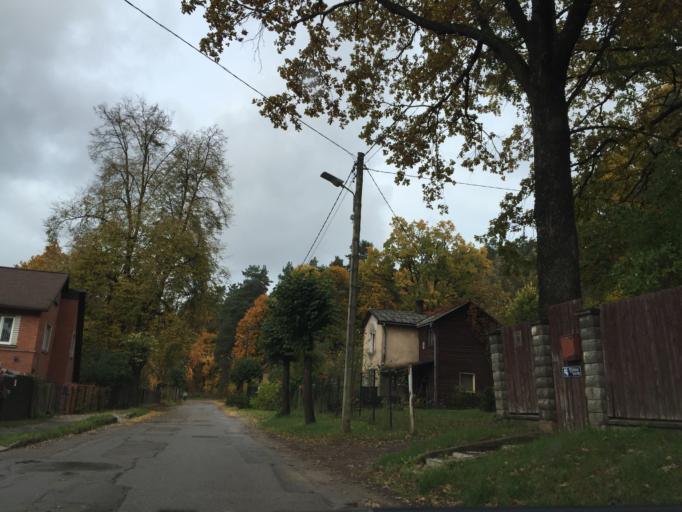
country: LV
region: Ogre
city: Ogre
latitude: 56.8110
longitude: 24.6168
